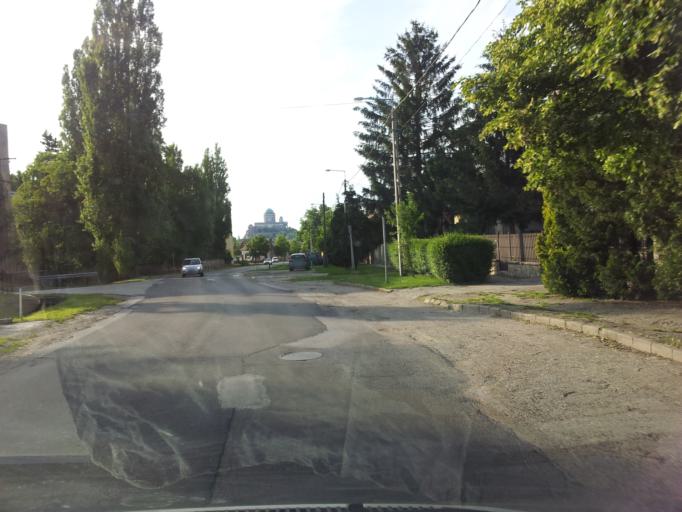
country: HU
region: Komarom-Esztergom
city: Esztergom
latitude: 47.7834
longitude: 18.7485
